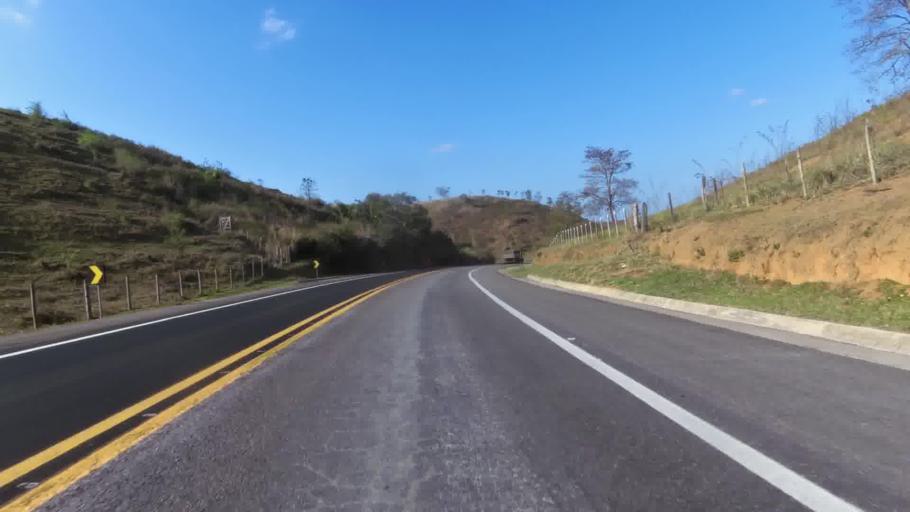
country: BR
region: Espirito Santo
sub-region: Mimoso Do Sul
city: Mimoso do Sul
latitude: -21.2292
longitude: -41.3163
